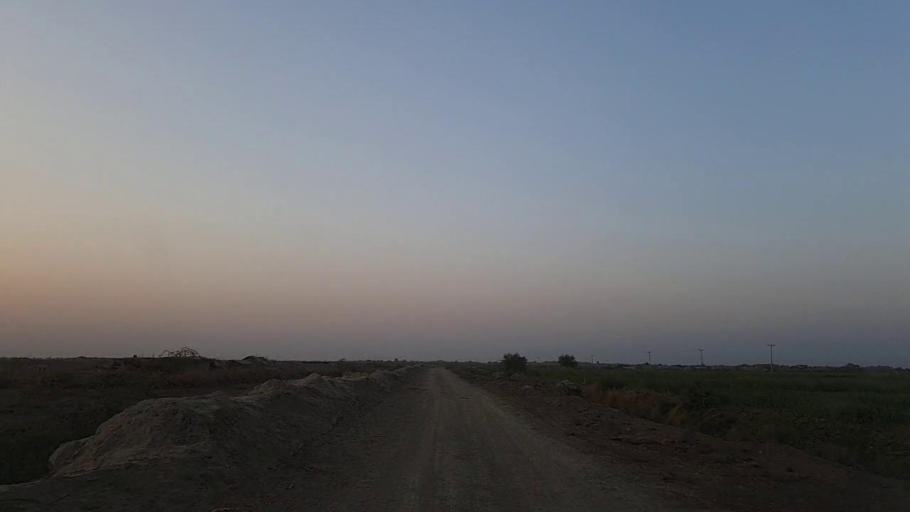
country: PK
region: Sindh
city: Naukot
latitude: 24.8957
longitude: 69.3591
